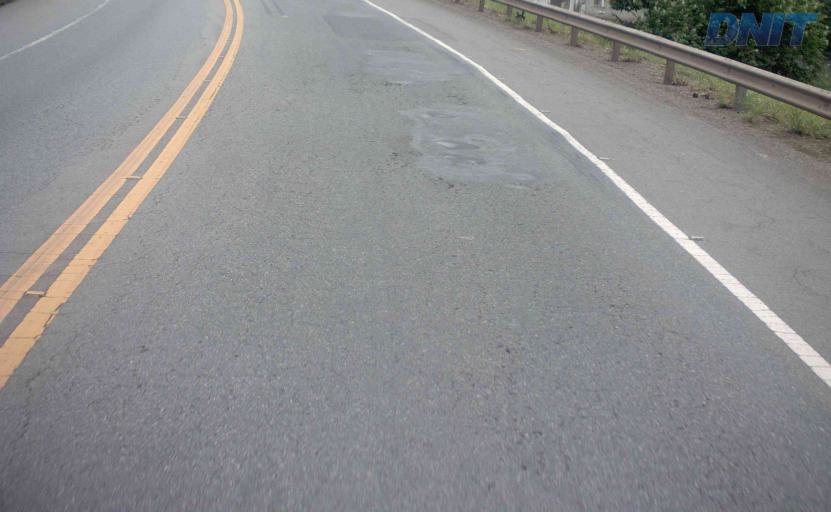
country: BR
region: Minas Gerais
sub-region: Coronel Fabriciano
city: Coronel Fabriciano
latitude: -19.5291
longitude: -42.6166
